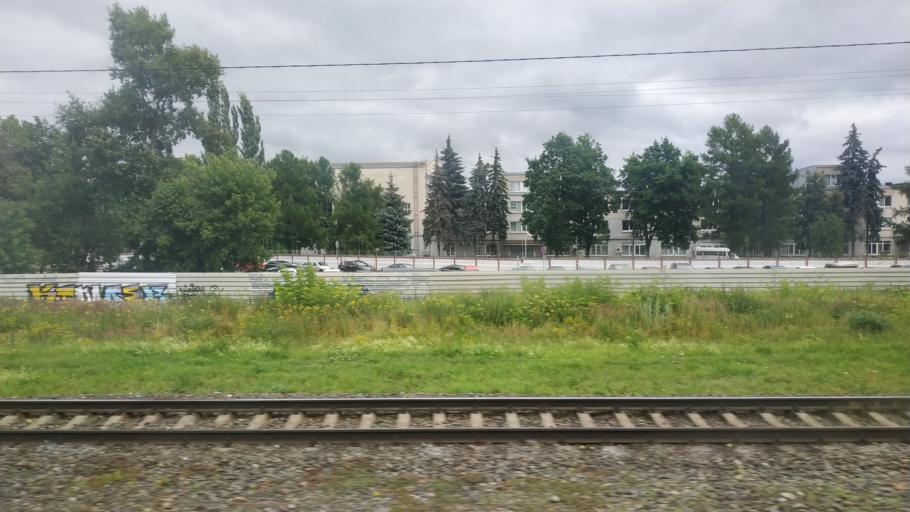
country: RU
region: Moskovskaya
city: Tomilino
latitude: 55.6651
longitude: 37.9313
